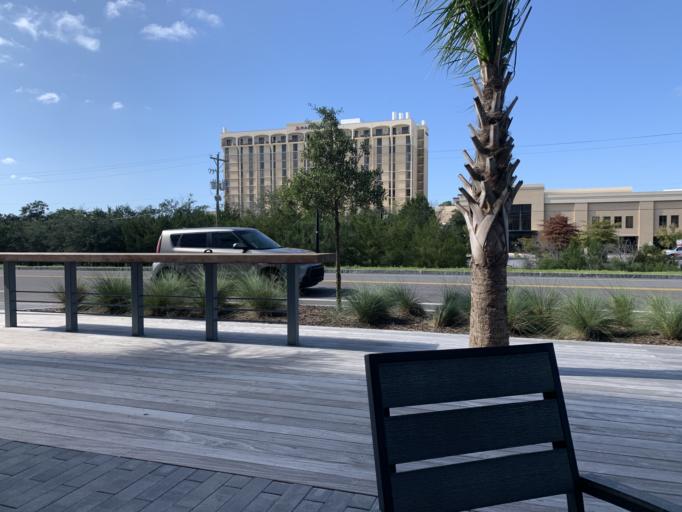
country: US
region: South Carolina
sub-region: Charleston County
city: Charleston
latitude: 32.7876
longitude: -79.9567
